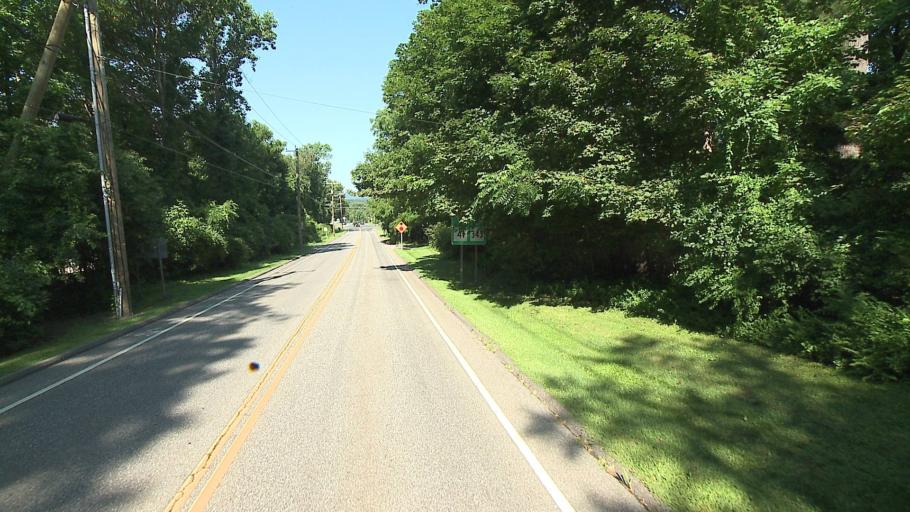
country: US
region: Connecticut
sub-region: Litchfield County
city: Kent
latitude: 41.8762
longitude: -73.4750
